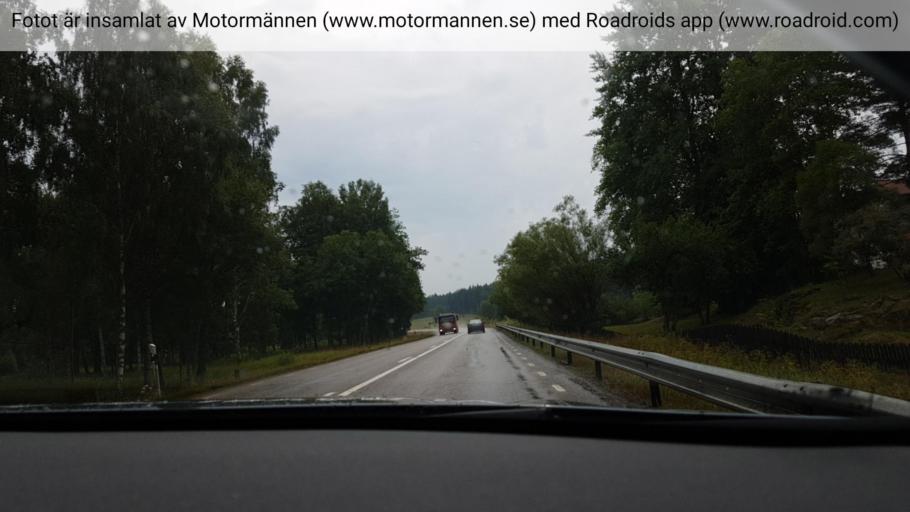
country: SE
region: Joenkoeping
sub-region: Vaggeryds Kommun
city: Vaggeryd
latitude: 57.5384
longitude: 14.2681
